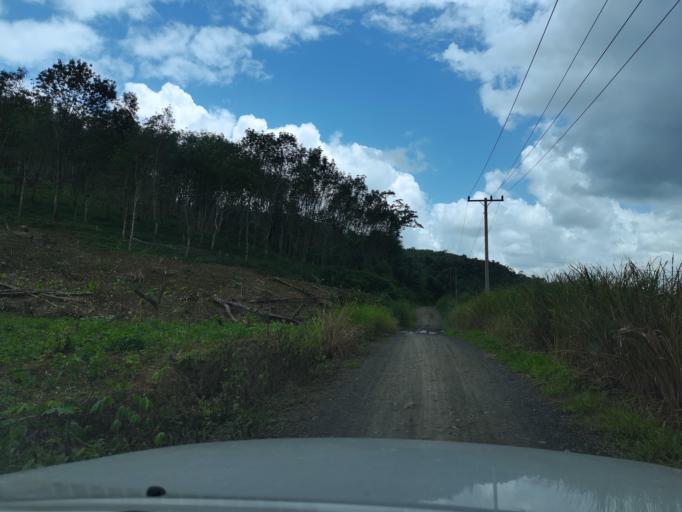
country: LA
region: Loungnamtha
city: Muang Long
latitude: 20.7721
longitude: 101.0167
